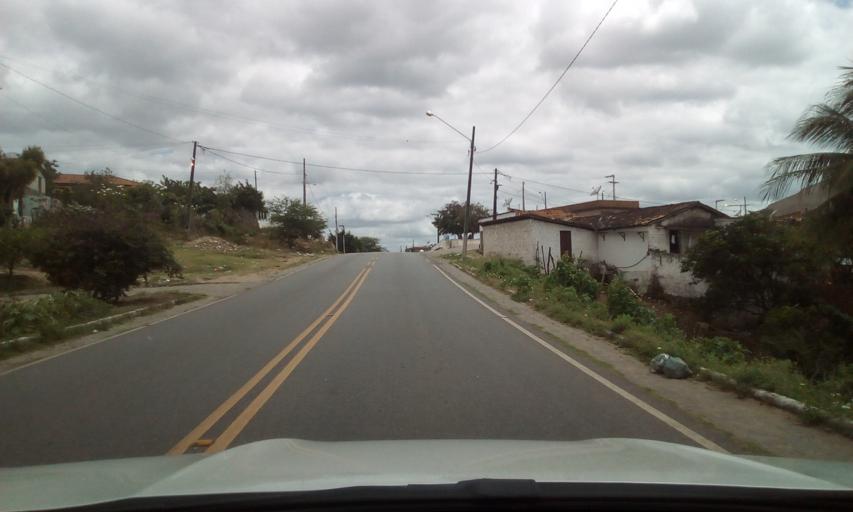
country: BR
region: Paraiba
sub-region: Serra Redonda
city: Alagoa Grande
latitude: -7.1764
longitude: -35.5903
